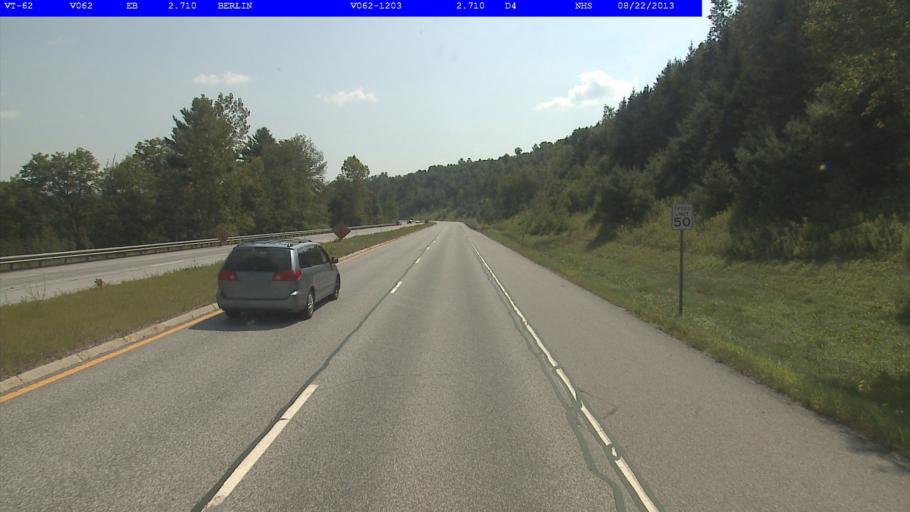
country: US
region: Vermont
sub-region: Washington County
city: Barre
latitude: 44.2143
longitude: -72.5379
